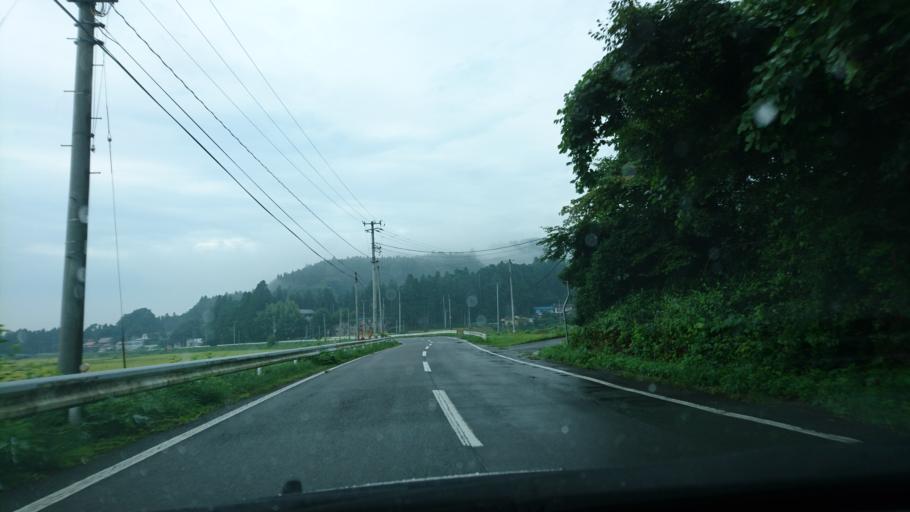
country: JP
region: Iwate
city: Ichinoseki
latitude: 38.8756
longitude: 141.2652
